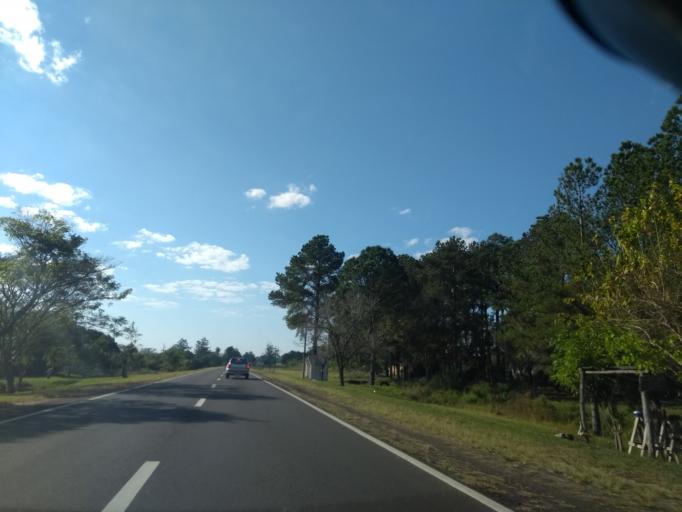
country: AR
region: Corrientes
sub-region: Departamento de Itati
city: Itati
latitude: -27.3660
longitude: -58.3079
